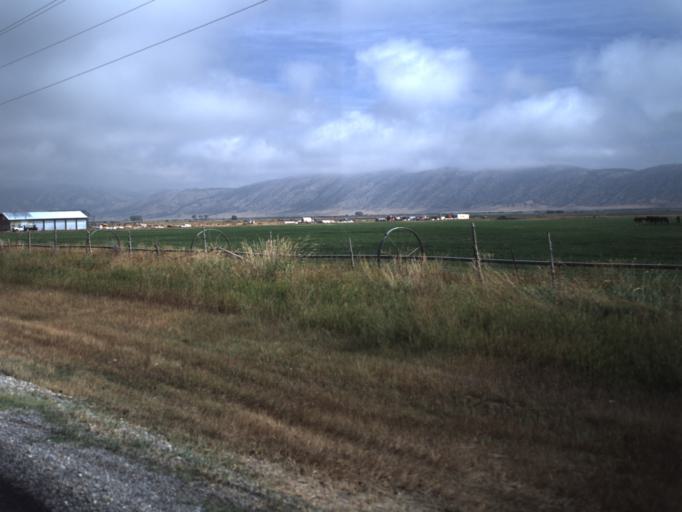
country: US
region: Utah
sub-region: Rich County
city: Randolph
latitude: 41.5277
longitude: -111.1629
